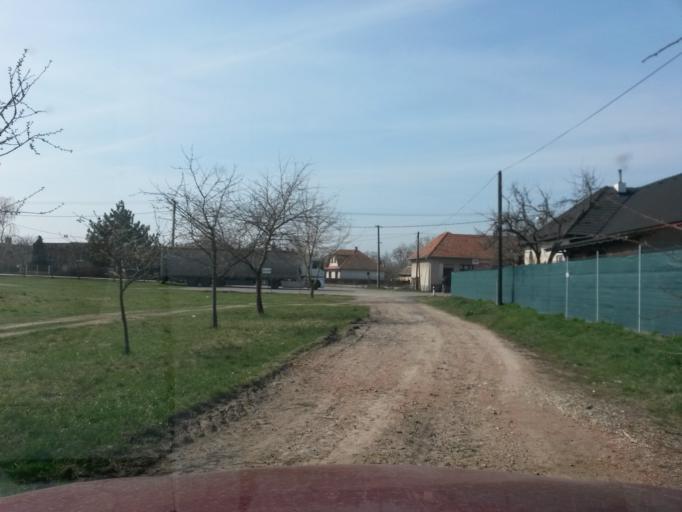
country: SK
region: Nitriansky
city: Levice
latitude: 48.1548
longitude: 18.5837
